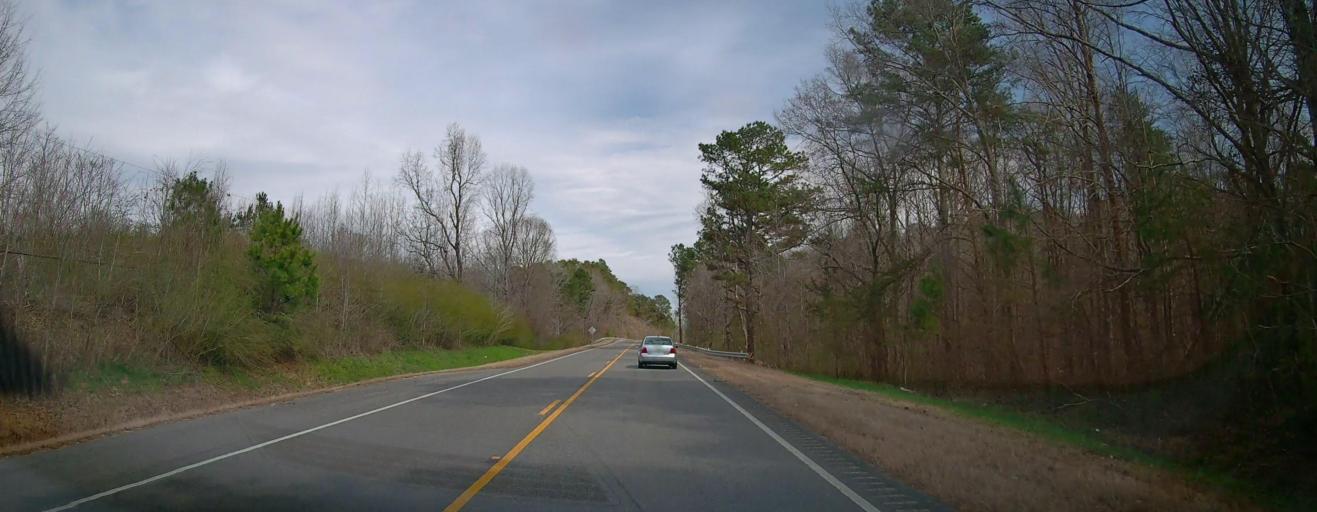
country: US
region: Alabama
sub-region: Walker County
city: Carbon Hill
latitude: 33.9177
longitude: -87.5729
